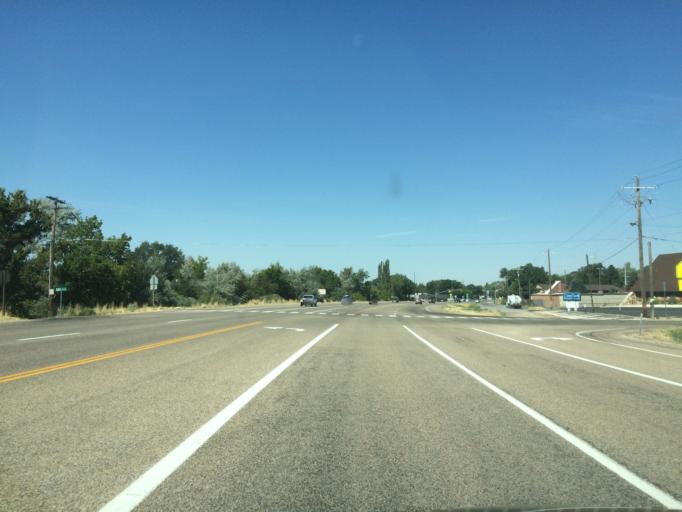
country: US
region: Utah
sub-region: Weber County
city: Ogden
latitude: 41.2405
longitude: -111.9413
